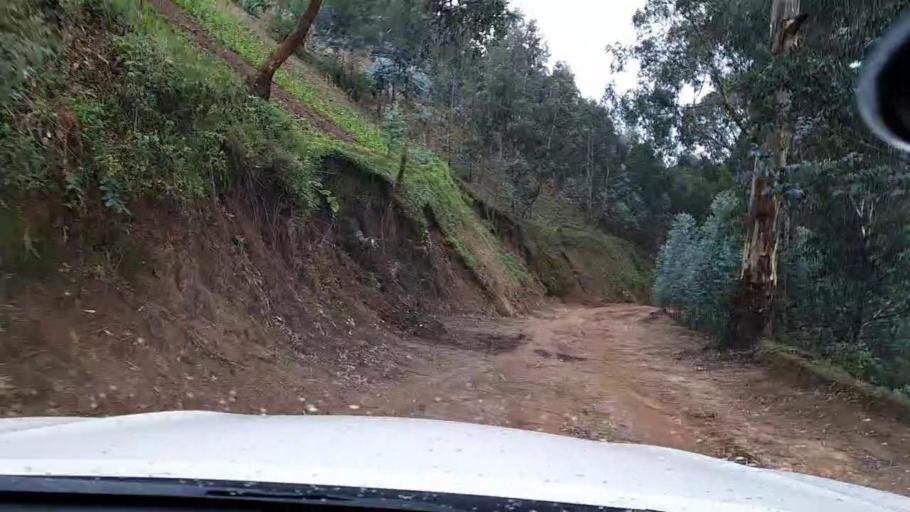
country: RW
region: Southern Province
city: Nzega
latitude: -2.3799
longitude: 29.2379
